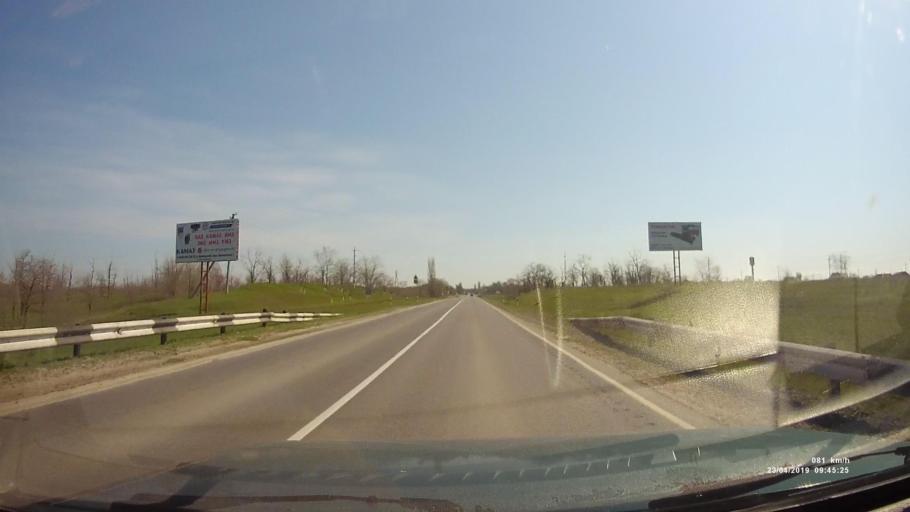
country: RU
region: Rostov
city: Orlovskiy
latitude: 46.8829
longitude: 42.0304
